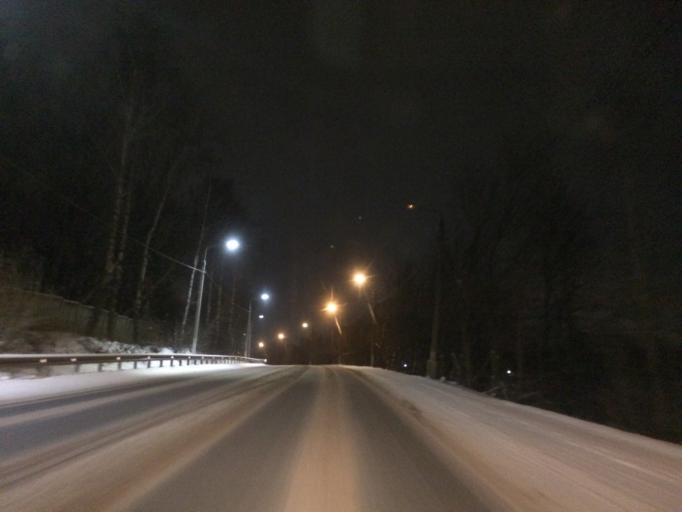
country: RU
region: Tula
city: Tula
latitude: 54.2226
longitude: 37.6509
